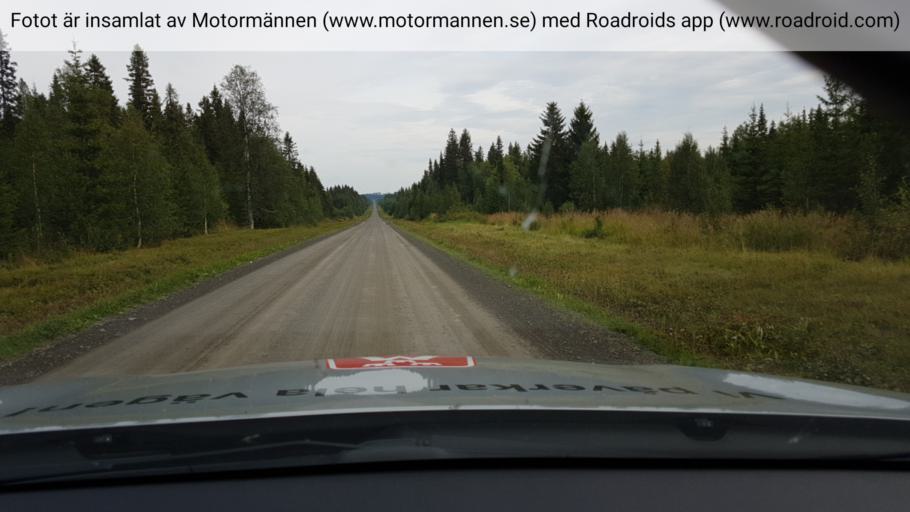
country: SE
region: Jaemtland
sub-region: OEstersunds Kommun
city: Lit
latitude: 63.6710
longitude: 14.8853
